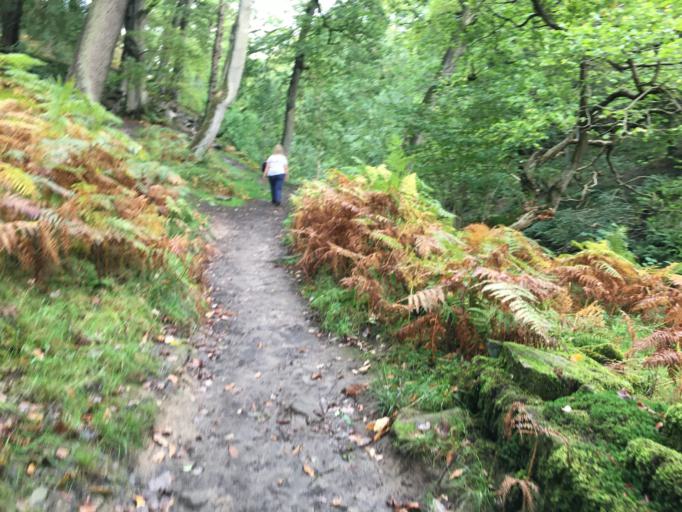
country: GB
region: England
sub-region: North Yorkshire
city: Sleights
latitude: 54.4084
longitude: -0.7304
